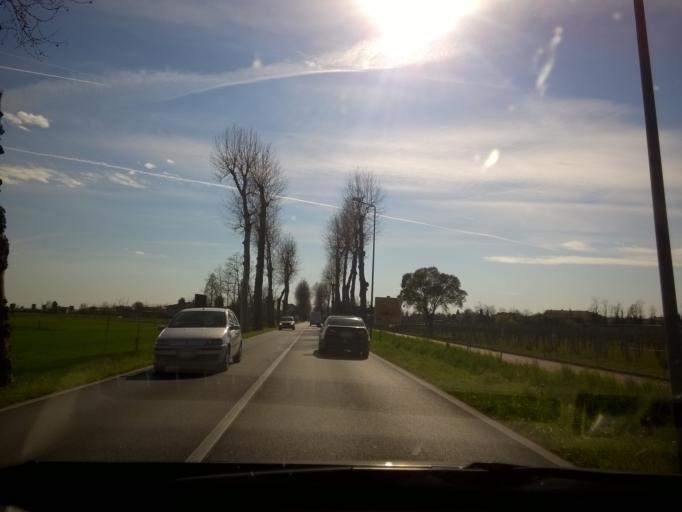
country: IT
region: Veneto
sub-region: Provincia di Treviso
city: Selva del Montello
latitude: 45.7816
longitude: 12.1329
